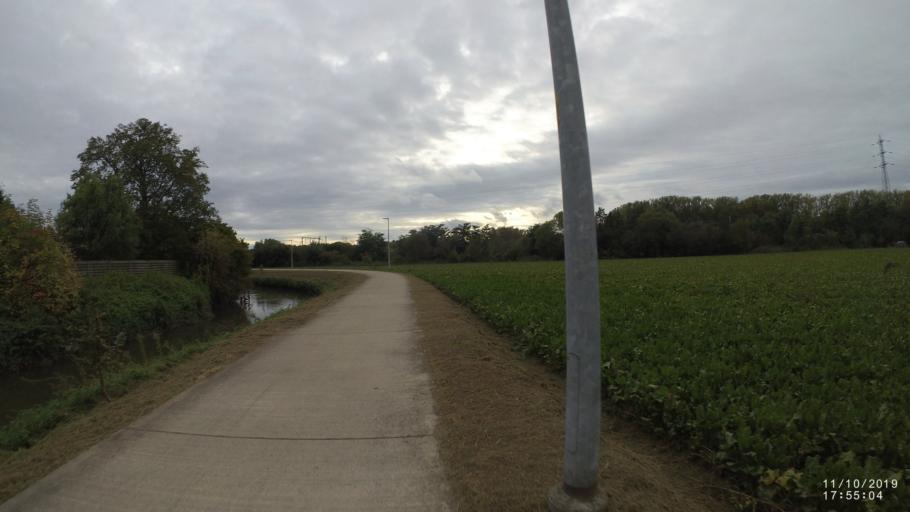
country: BE
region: Flanders
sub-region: Provincie Vlaams-Brabant
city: Leuven
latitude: 50.9090
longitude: 4.7104
